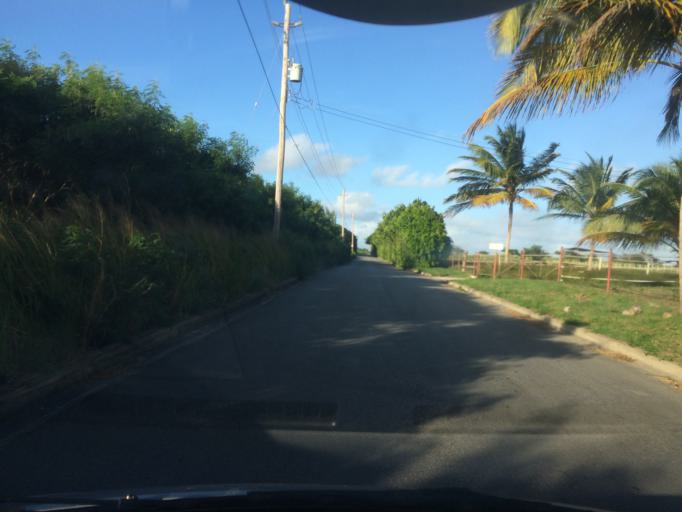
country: BB
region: Saint Lucy
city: Checker Hall
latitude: 13.3002
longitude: -59.6424
